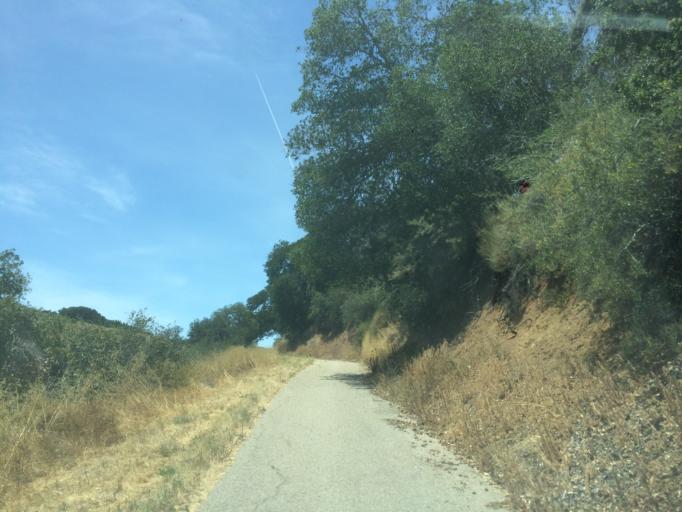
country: US
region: California
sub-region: San Luis Obispo County
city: San Luis Obispo
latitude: 35.2546
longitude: -120.7002
